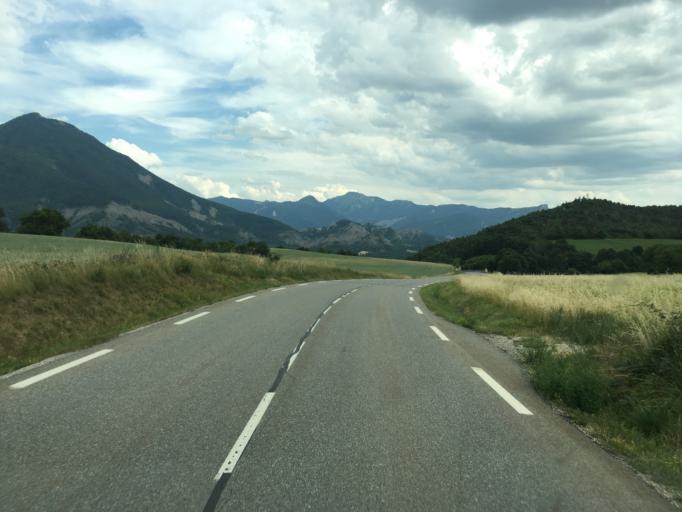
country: FR
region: Provence-Alpes-Cote d'Azur
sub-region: Departement des Hautes-Alpes
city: Veynes
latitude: 44.5344
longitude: 5.7969
